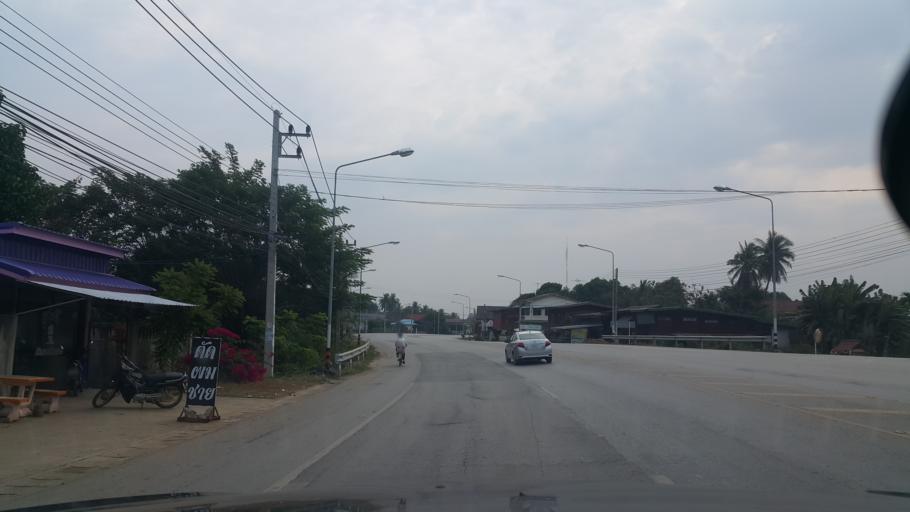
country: TH
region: Sukhothai
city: Si Samrong
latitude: 17.1610
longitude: 99.8659
